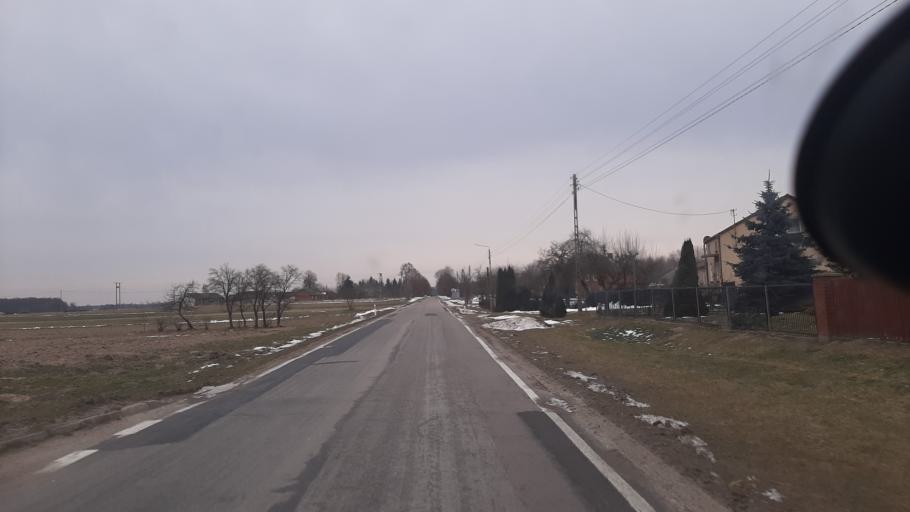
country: PL
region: Lublin Voivodeship
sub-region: Powiat lubartowski
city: Kamionka
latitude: 51.4636
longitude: 22.4202
